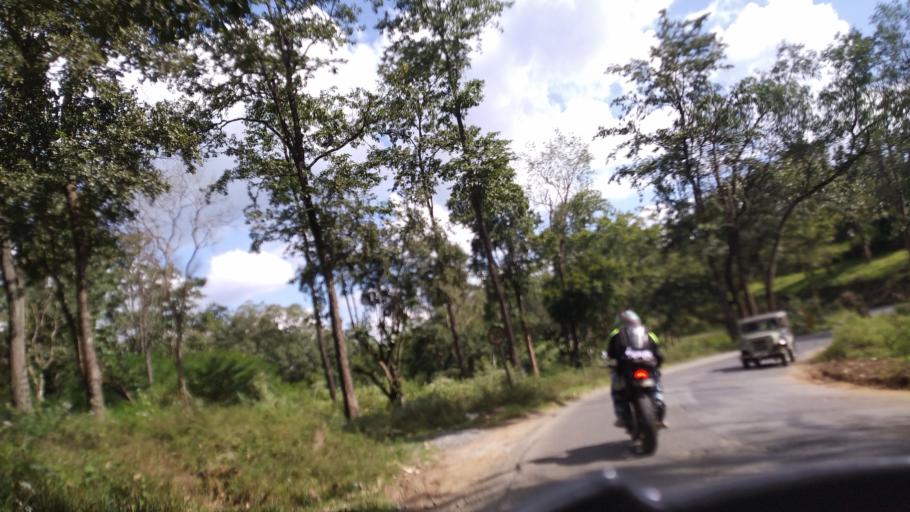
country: IN
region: Kerala
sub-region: Wayanad
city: Panamaram
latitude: 11.9335
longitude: 76.0647
